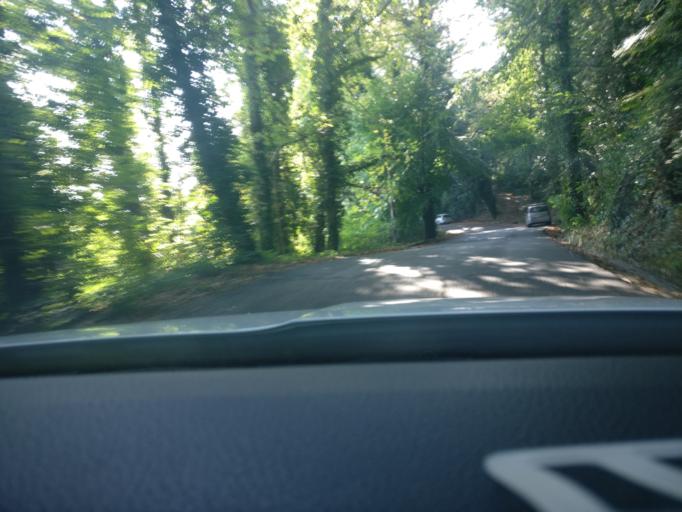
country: GR
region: Thessaly
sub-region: Nomos Magnisias
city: Zagora
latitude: 39.3845
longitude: 23.1791
